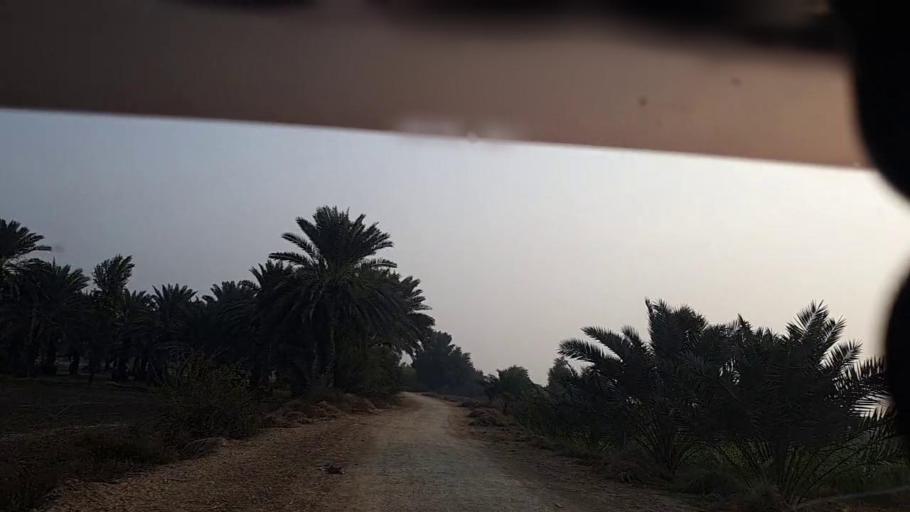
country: PK
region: Sindh
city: Gambat
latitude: 27.4340
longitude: 68.5976
